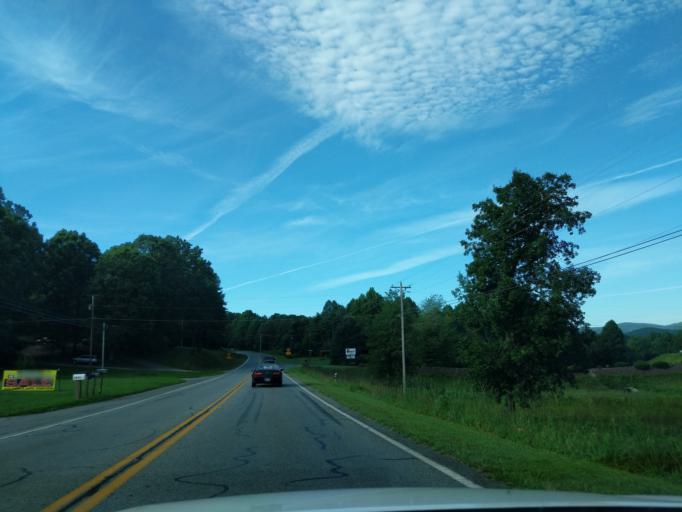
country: US
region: Georgia
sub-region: Fannin County
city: Blue Ridge
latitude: 34.9124
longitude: -84.3764
